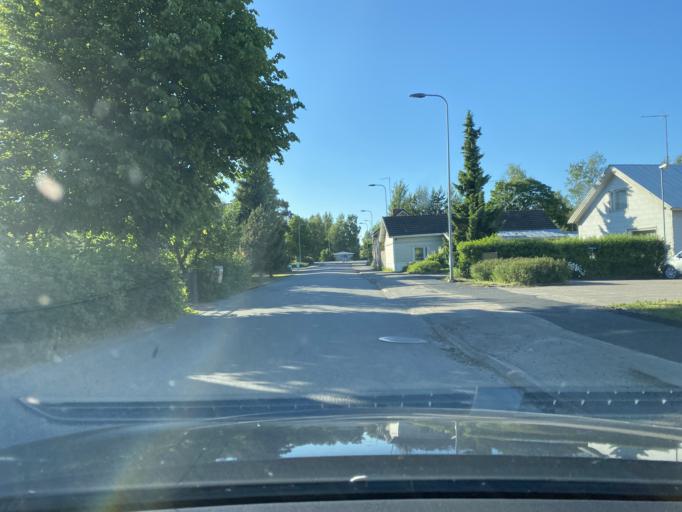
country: FI
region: Satakunta
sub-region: Pori
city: Huittinen
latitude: 61.1732
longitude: 22.6952
